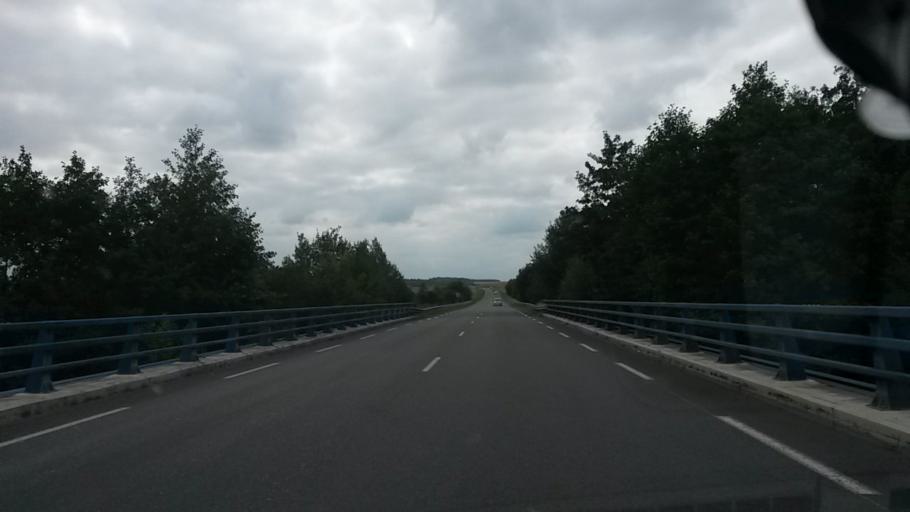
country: FR
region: Picardie
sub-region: Departement de la Somme
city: Corbie
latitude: 49.9503
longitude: 2.4409
